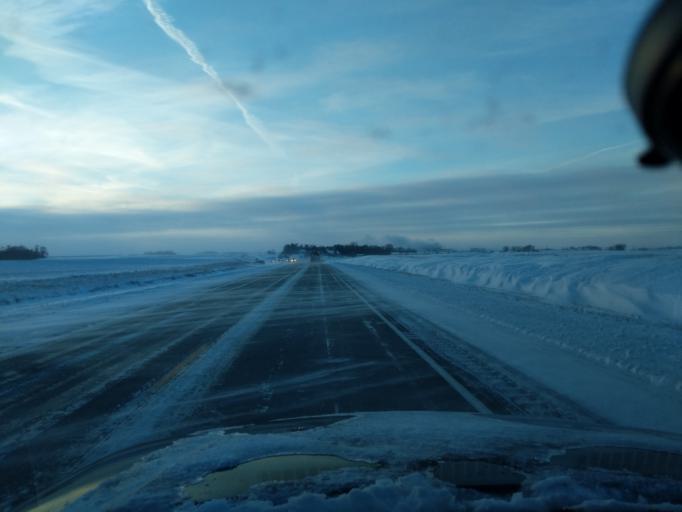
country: US
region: Minnesota
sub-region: Renville County
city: Renville
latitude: 44.7894
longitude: -95.1302
